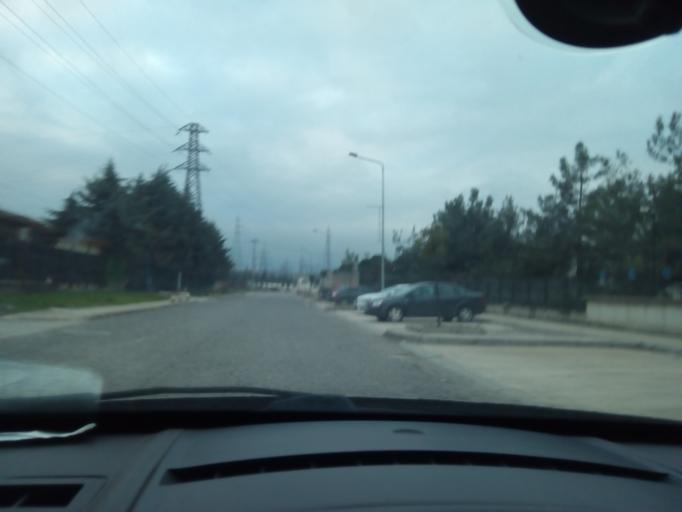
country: TR
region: Bursa
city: Niluefer
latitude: 40.2368
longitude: 28.9682
